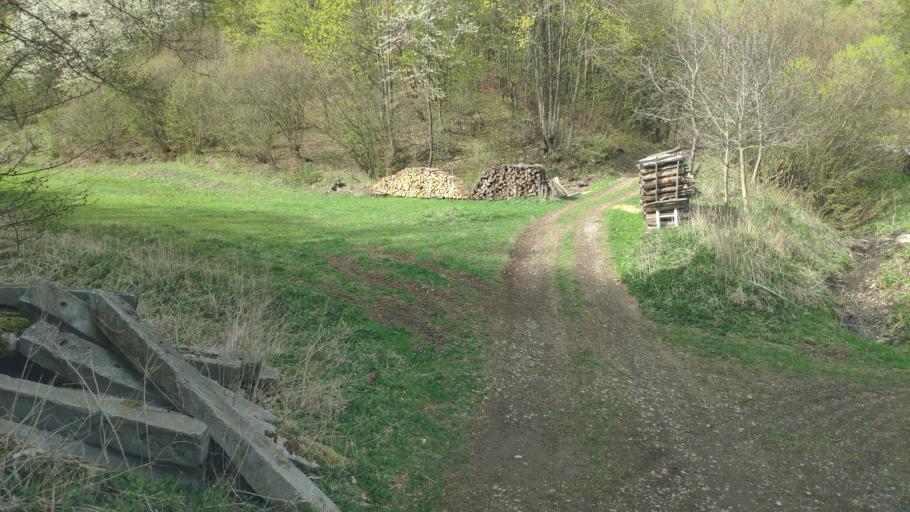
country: SK
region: Kosicky
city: Medzev
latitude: 48.6700
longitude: 20.8331
